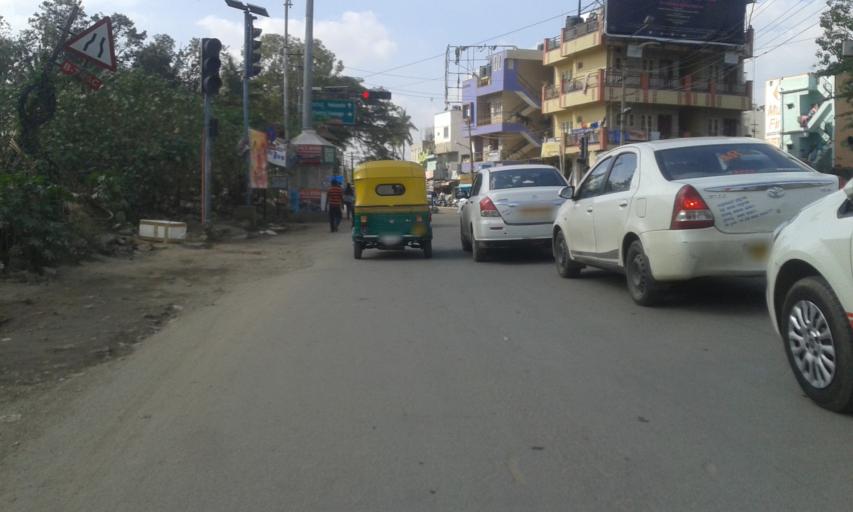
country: IN
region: Karnataka
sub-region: Bangalore Urban
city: Bangalore
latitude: 12.9522
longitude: 77.6204
